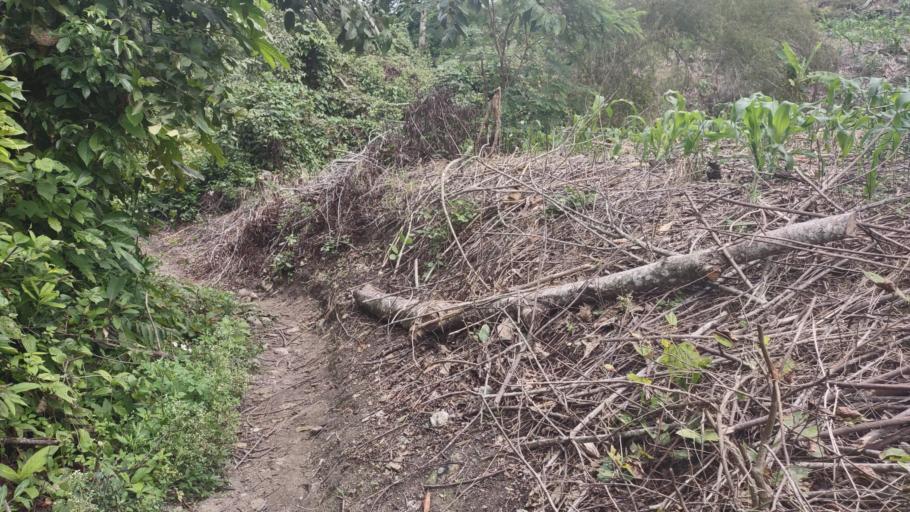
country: MX
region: Veracruz
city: Papantla de Olarte
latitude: 20.4349
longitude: -97.2606
